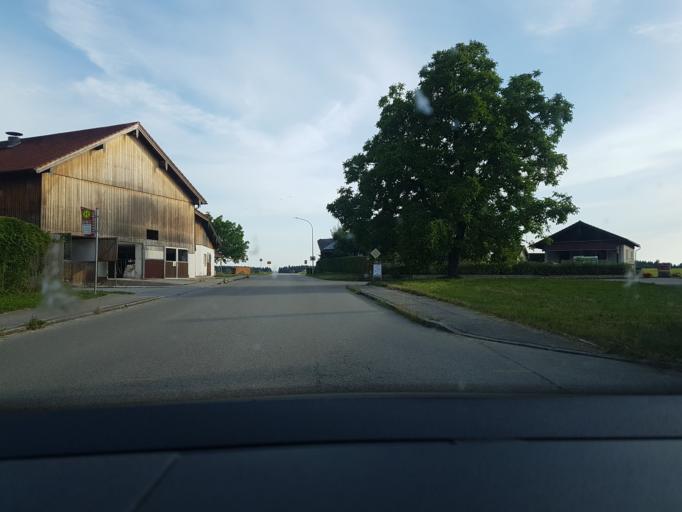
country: DE
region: Bavaria
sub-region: Upper Bavaria
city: Anger
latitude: 47.8459
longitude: 12.8768
